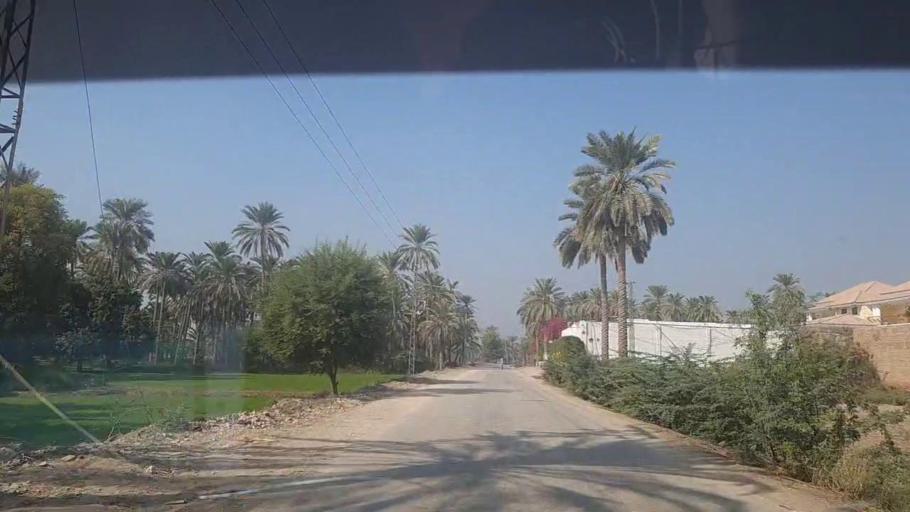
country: PK
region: Sindh
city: Kot Diji
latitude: 27.3797
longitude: 68.6906
